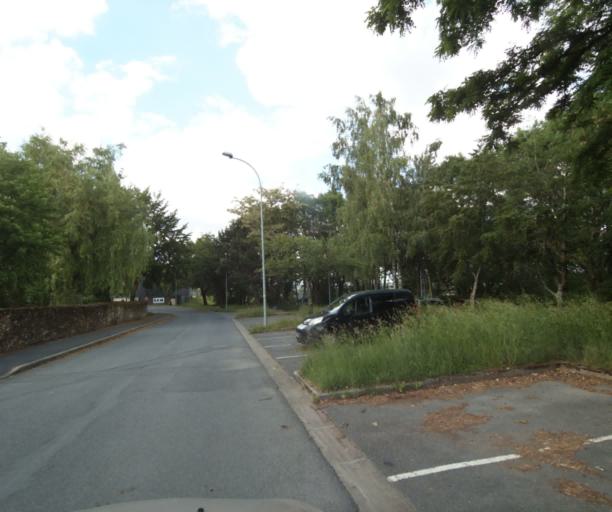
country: FR
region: Champagne-Ardenne
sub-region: Departement des Ardennes
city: Montcy-Notre-Dame
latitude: 49.7622
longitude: 4.7422
